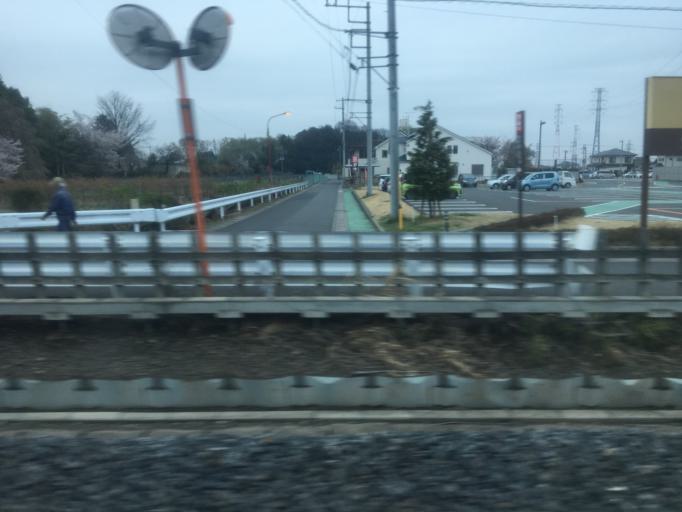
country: JP
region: Saitama
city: Okegawa
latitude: 36.0164
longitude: 139.5461
